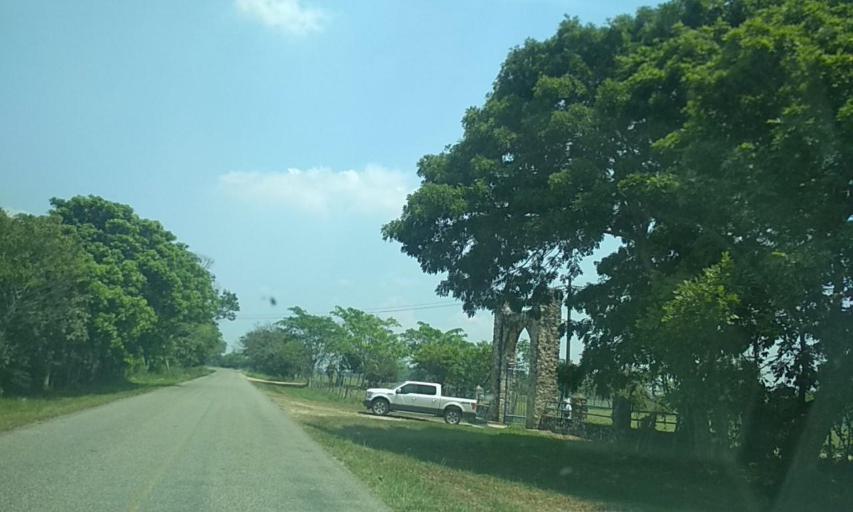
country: MX
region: Tabasco
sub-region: Cardenas
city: Poblado C-33 20 de Noviembre
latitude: 17.8421
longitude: -93.5622
